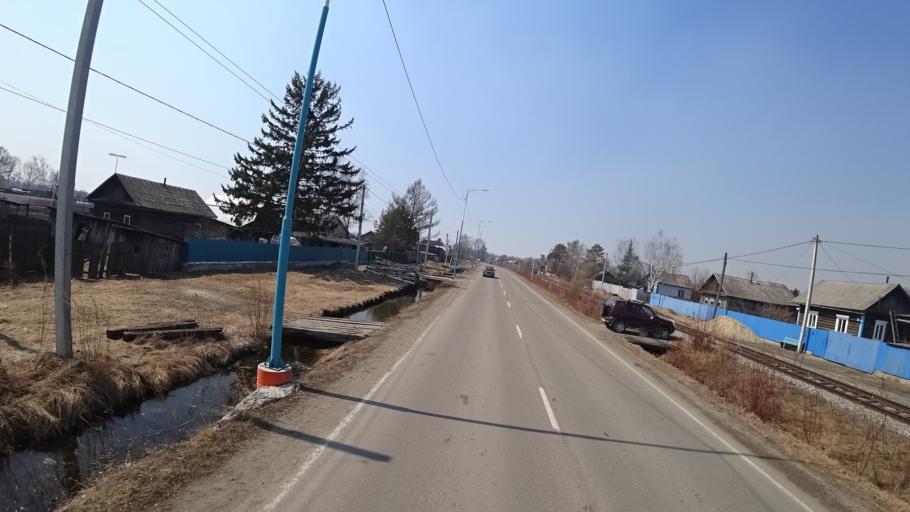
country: RU
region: Amur
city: Novobureyskiy
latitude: 49.7942
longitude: 129.8960
